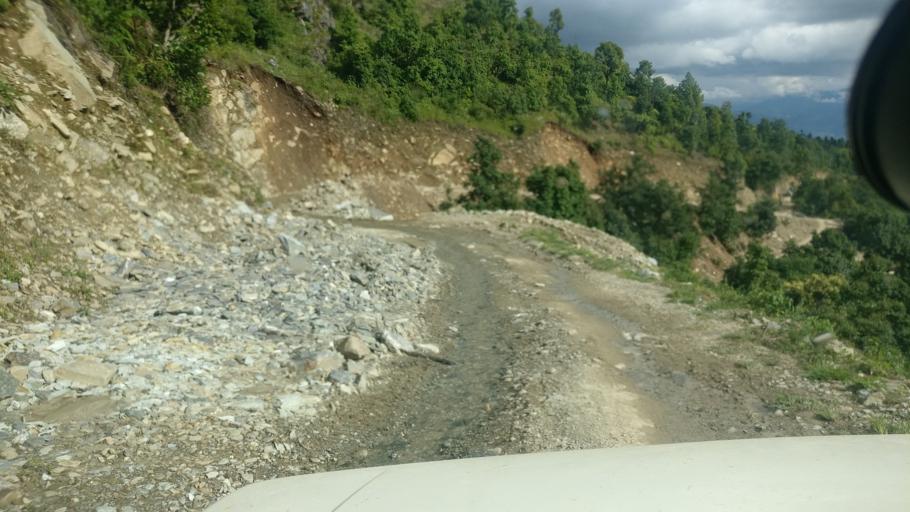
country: NP
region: Western Region
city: Baglung
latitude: 28.2747
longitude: 83.6428
